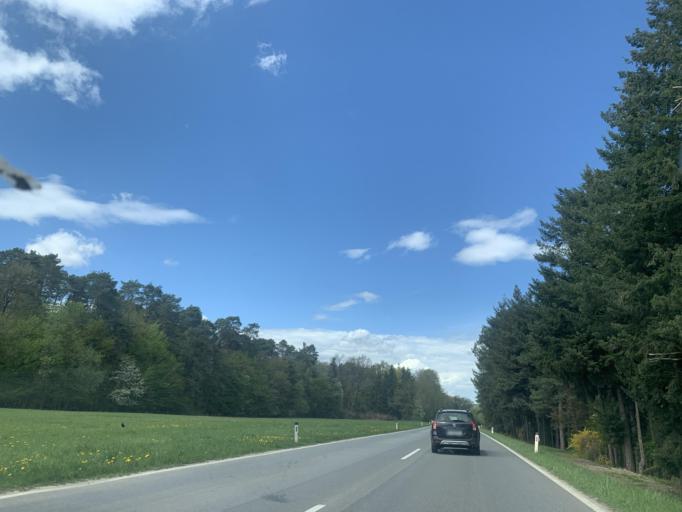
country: AT
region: Styria
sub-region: Politischer Bezirk Leibnitz
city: Lang
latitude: 46.8243
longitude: 15.5226
